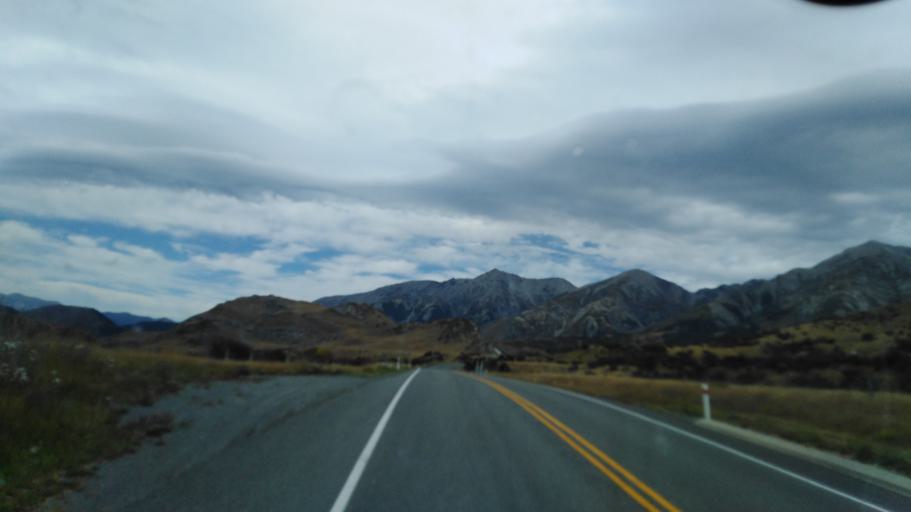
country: NZ
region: Canterbury
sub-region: Ashburton District
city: Methven
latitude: -43.2122
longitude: 171.7238
